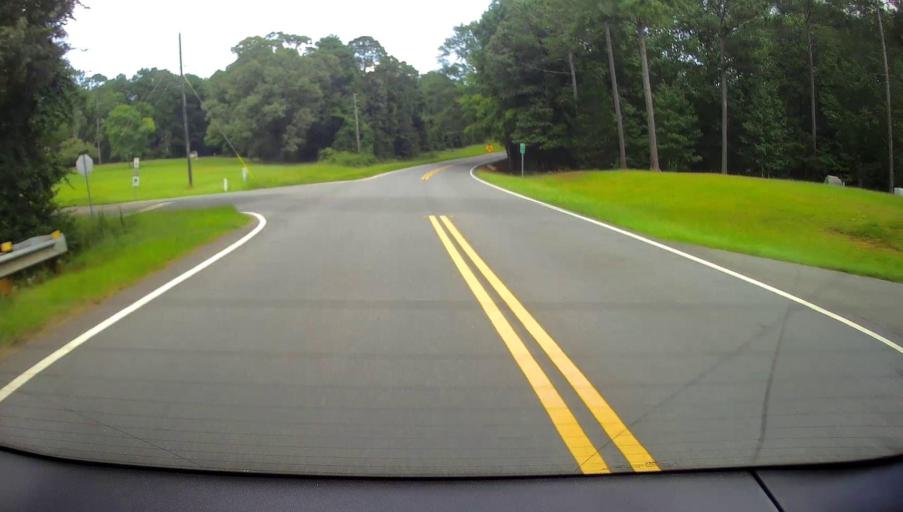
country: US
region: Georgia
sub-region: Monroe County
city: Forsyth
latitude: 32.8836
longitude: -83.9717
